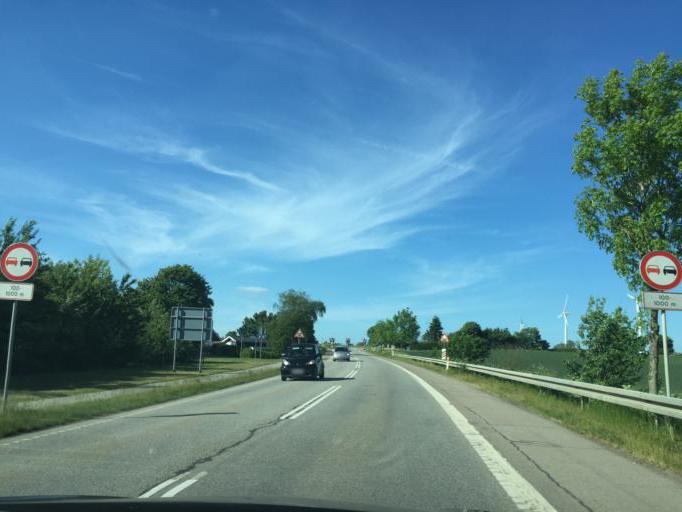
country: DK
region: Zealand
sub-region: Stevns Kommune
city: Harlev
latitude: 55.3529
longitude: 12.2487
